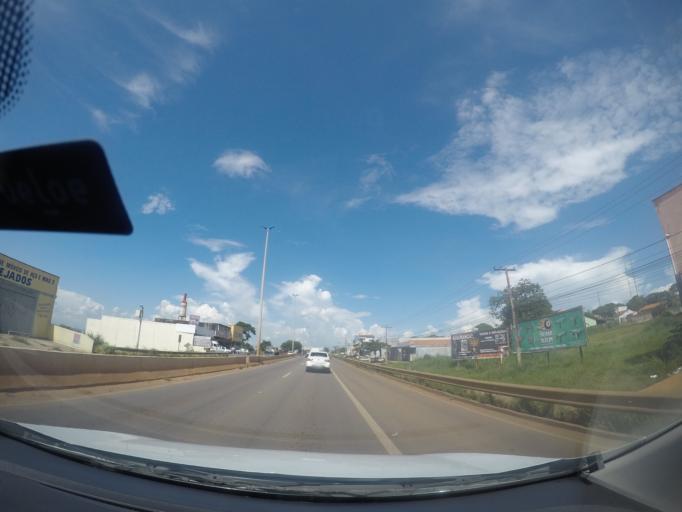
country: BR
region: Goias
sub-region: Goiania
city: Goiania
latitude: -16.6599
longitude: -49.3419
